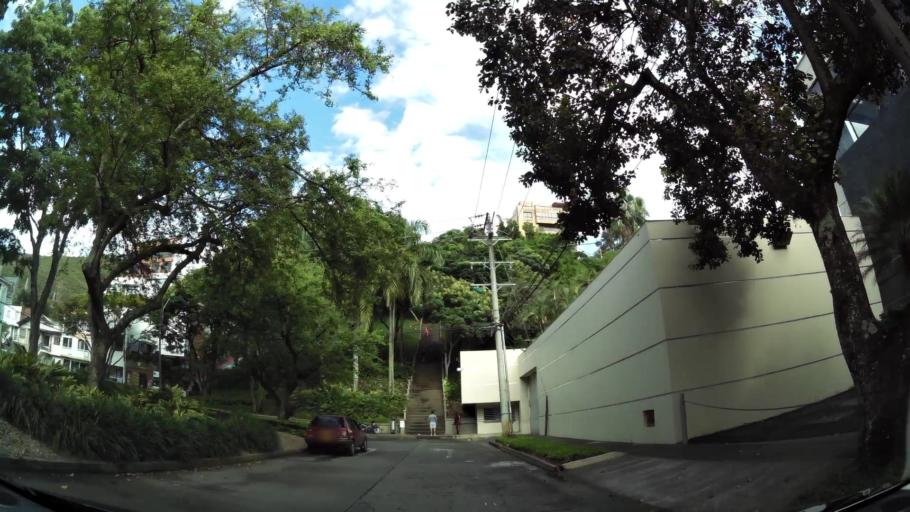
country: CO
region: Valle del Cauca
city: Cali
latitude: 3.4718
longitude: -76.5303
